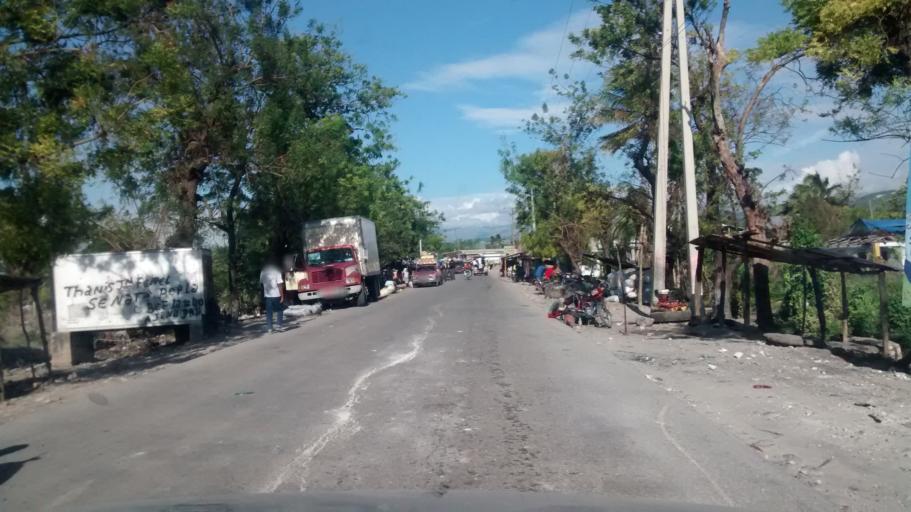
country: HT
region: Sud
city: Cavaillon
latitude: 18.2974
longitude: -73.6538
